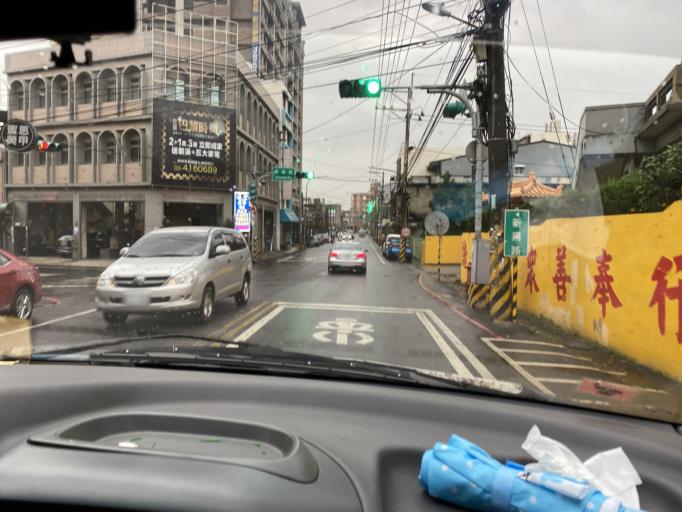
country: TW
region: Taiwan
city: Taoyuan City
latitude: 25.0571
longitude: 121.1966
